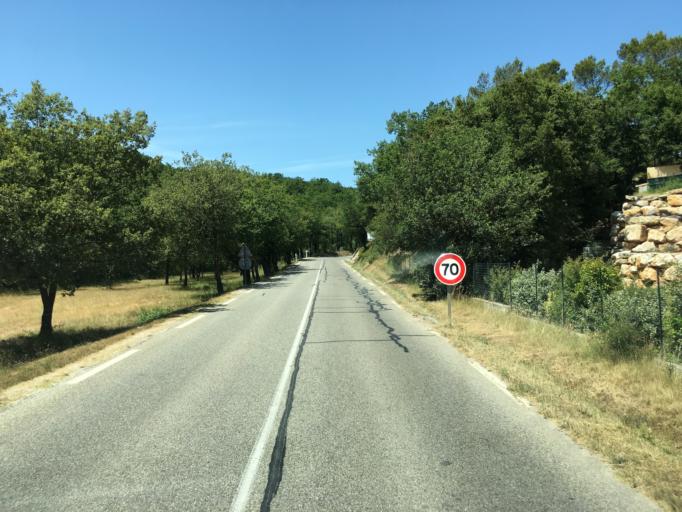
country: FR
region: Provence-Alpes-Cote d'Azur
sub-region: Departement du Var
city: Saint-Maximin-la-Sainte-Baume
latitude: 43.4786
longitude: 5.8331
